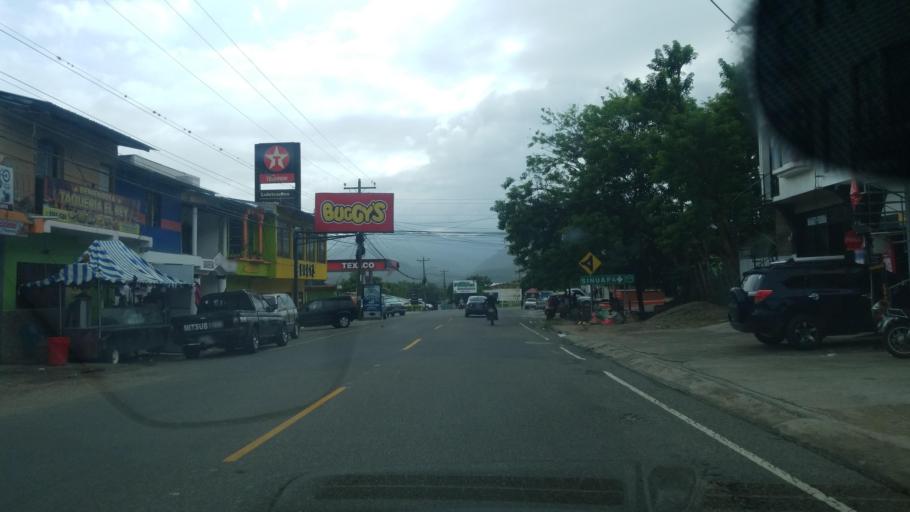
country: HN
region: Ocotepeque
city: Sinuapa
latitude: 14.4418
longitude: -89.1819
